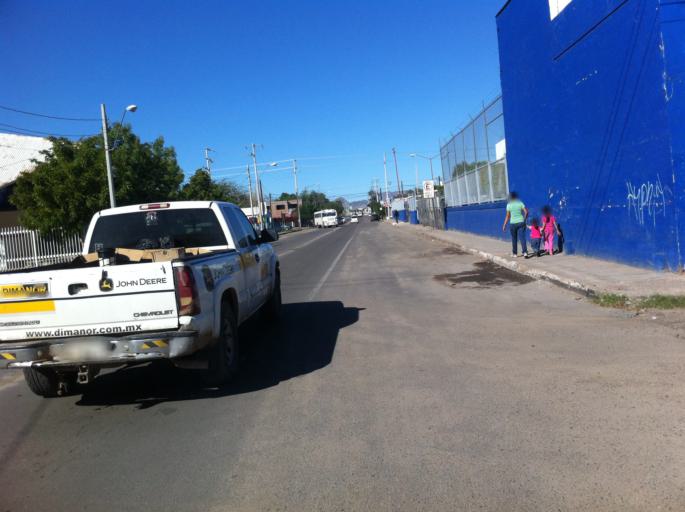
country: MX
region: Sonora
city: Hermosillo
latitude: 29.1088
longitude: -111.0055
